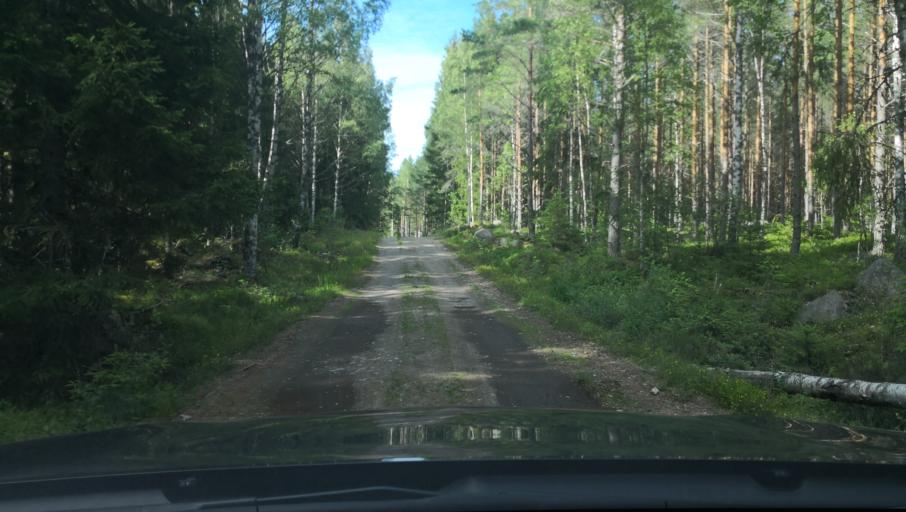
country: SE
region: Vaestmanland
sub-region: Surahammars Kommun
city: Surahammar
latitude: 59.6703
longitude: 16.1083
